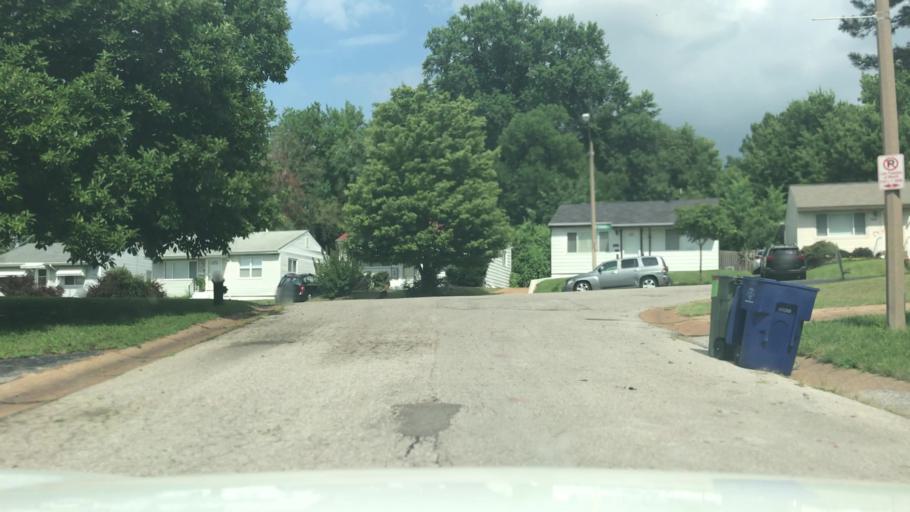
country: US
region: Missouri
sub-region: Saint Louis County
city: Richmond Heights
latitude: 38.6143
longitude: -90.2963
